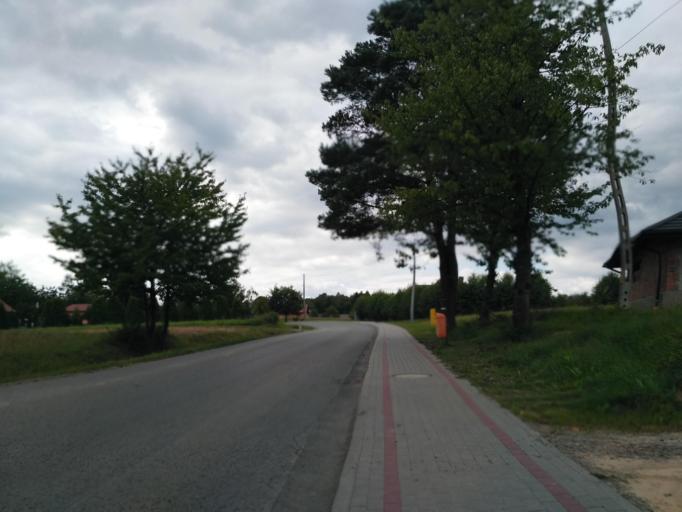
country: PL
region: Subcarpathian Voivodeship
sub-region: Powiat rzeszowski
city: Lecka
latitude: 49.8921
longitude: 21.9999
